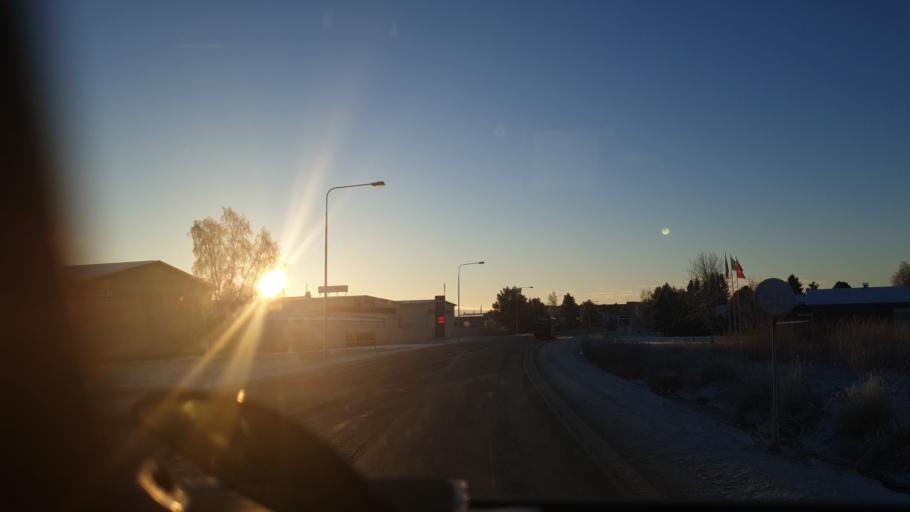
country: FI
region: Northern Ostrobothnia
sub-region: Ylivieska
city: Kalajoki
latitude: 64.2639
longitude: 23.9492
